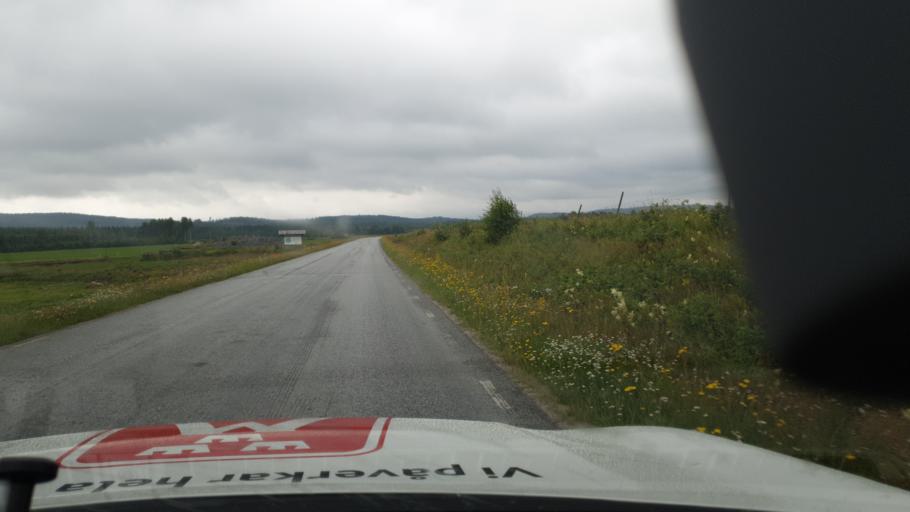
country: SE
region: Vaesterbotten
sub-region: Vannas Kommun
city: Vannasby
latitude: 63.9271
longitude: 19.8382
